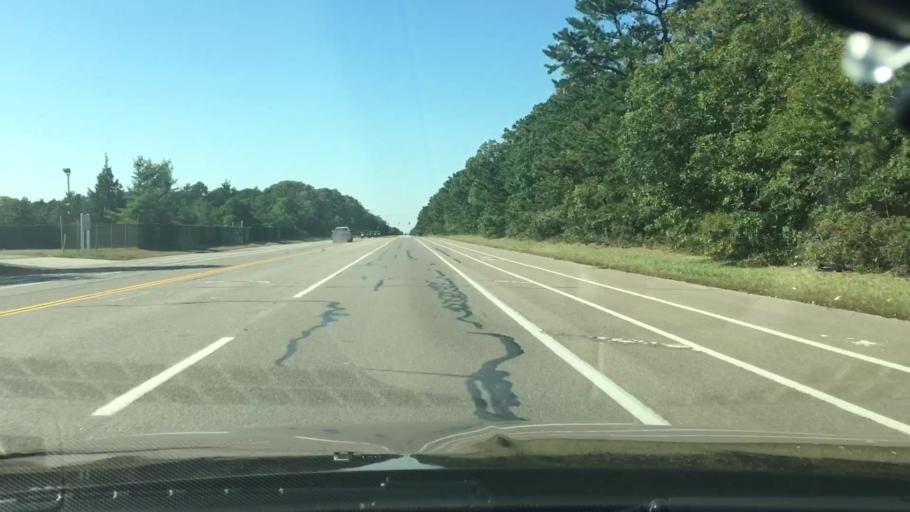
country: US
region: New York
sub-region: Suffolk County
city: North Bellport
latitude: 40.7967
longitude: -72.9692
